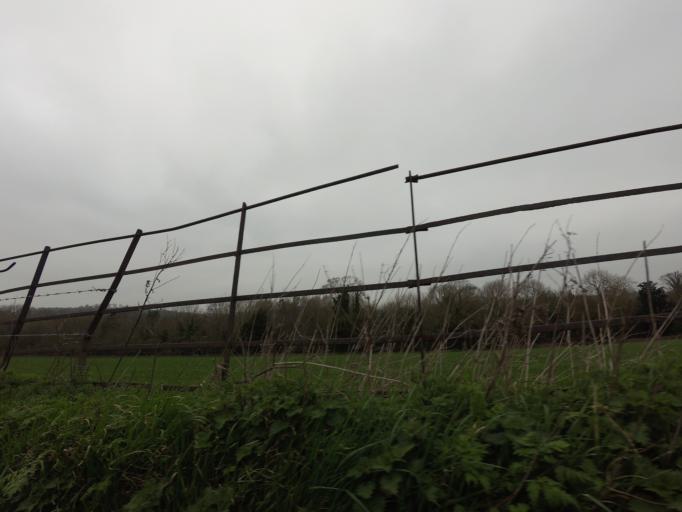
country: GB
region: England
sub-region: Kent
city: Eynsford
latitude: 51.3558
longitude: 0.1983
